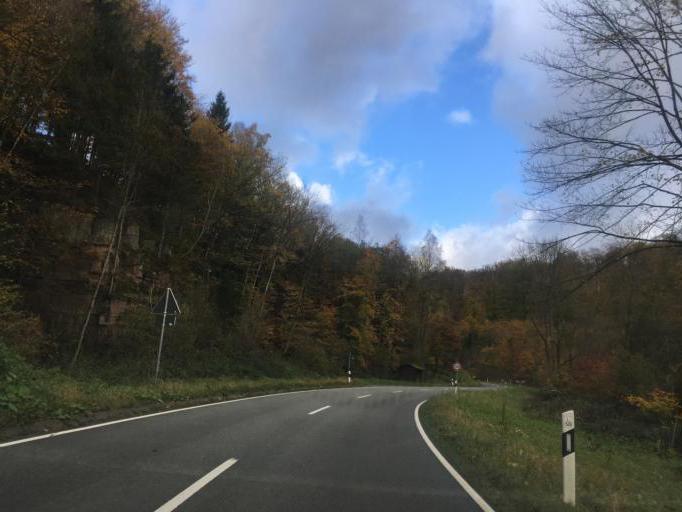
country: DE
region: Lower Saxony
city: Furstenberg
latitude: 51.7455
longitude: 9.4291
